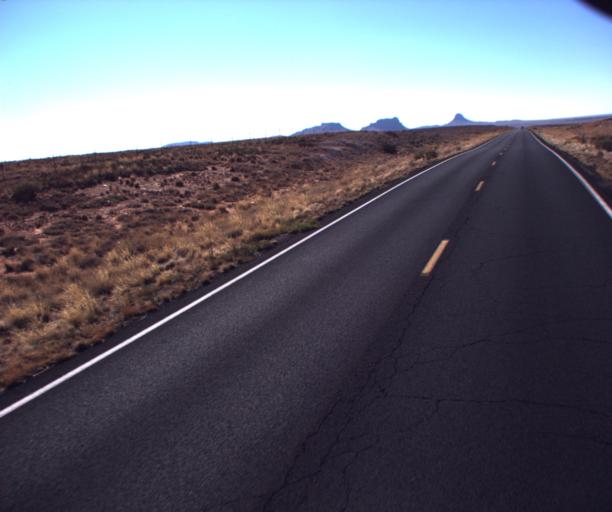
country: US
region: Arizona
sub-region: Navajo County
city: Dilkon
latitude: 35.4070
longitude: -110.4264
